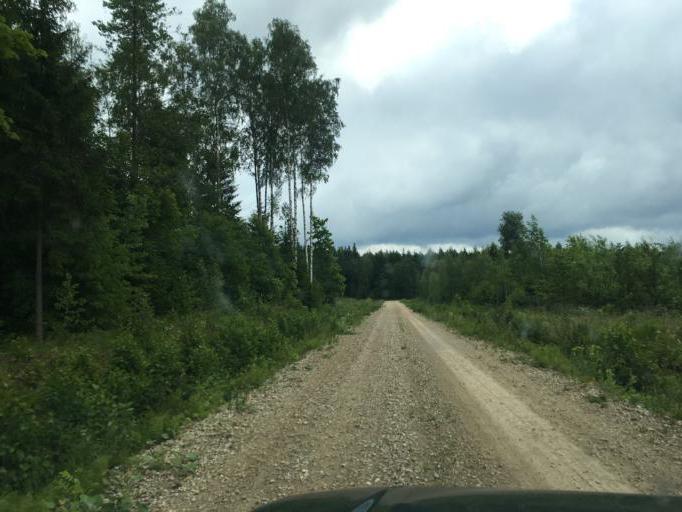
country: LV
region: Vilaka
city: Vilaka
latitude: 57.3875
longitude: 27.5165
